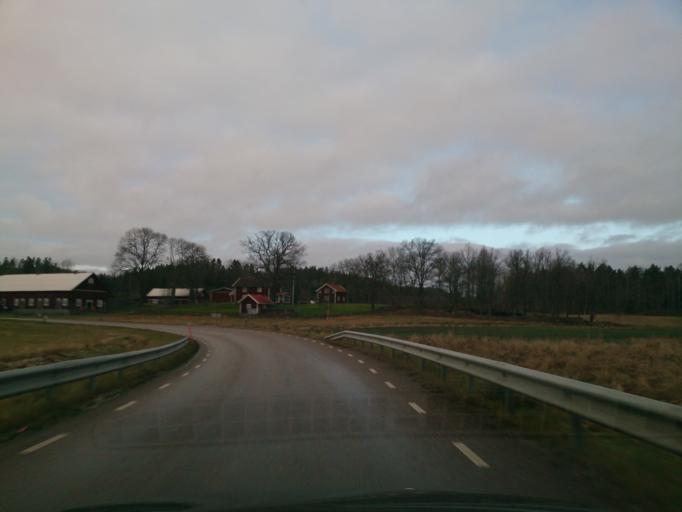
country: SE
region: OEstergoetland
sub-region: Atvidabergs Kommun
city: Atvidaberg
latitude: 58.2844
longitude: 16.0352
